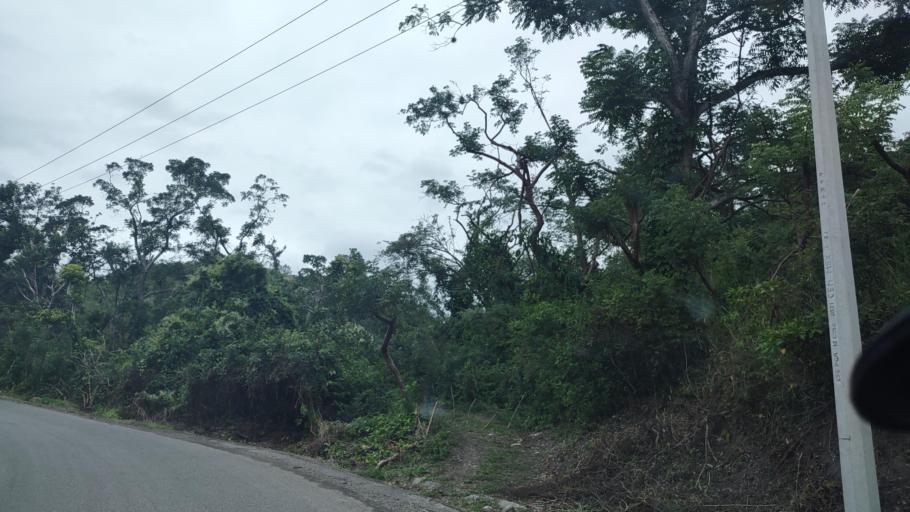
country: MX
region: Veracruz
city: Papantla de Olarte
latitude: 20.4456
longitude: -97.2959
